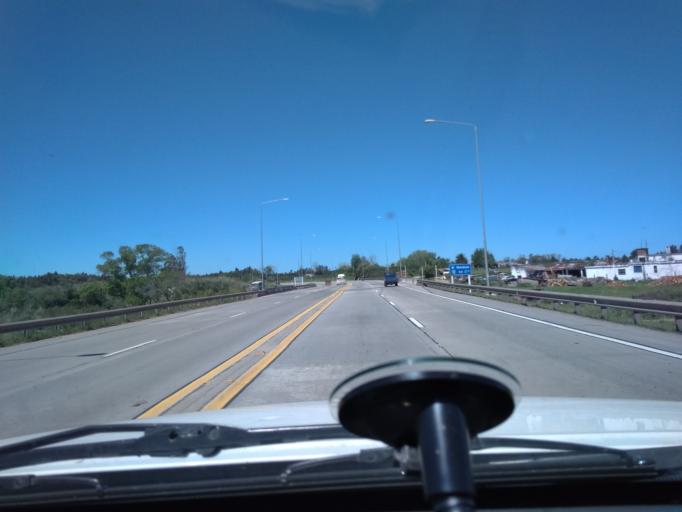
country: UY
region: Canelones
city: La Paz
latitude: -34.7967
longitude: -56.1603
